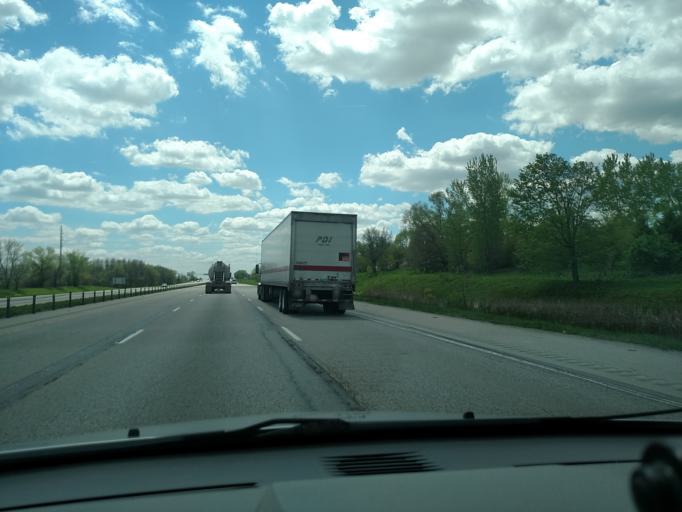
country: US
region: Iowa
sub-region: Polk County
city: Ankeny
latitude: 41.7196
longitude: -93.5767
